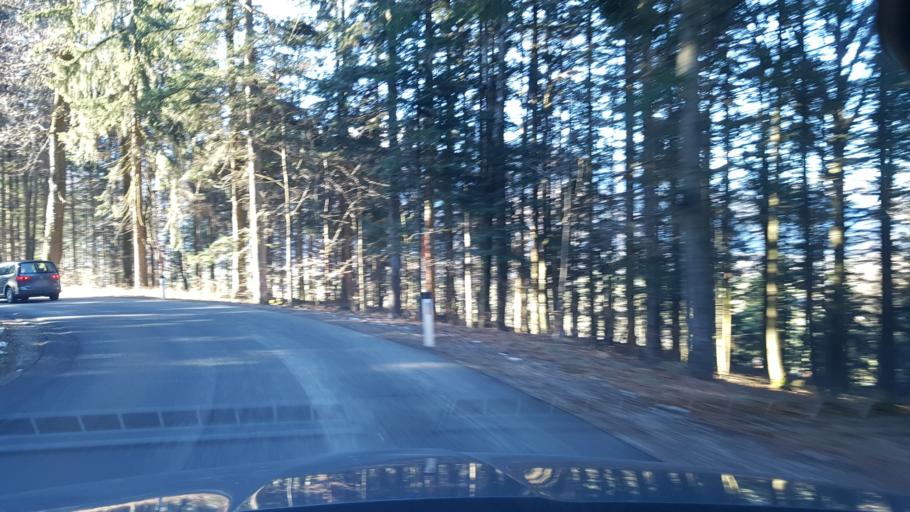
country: AT
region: Salzburg
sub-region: Politischer Bezirk Hallein
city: Golling an der Salzach
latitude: 47.6206
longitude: 13.1732
